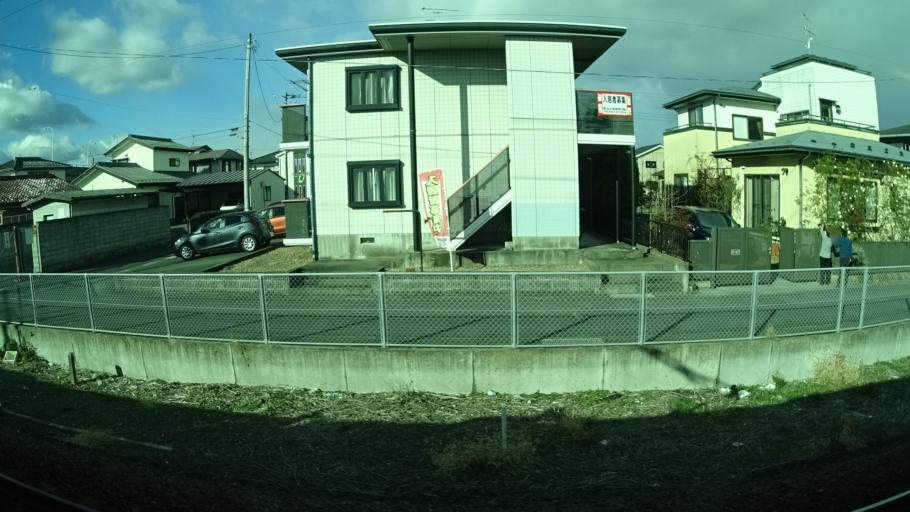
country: JP
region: Miyagi
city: Iwanuma
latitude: 38.1172
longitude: 140.8680
